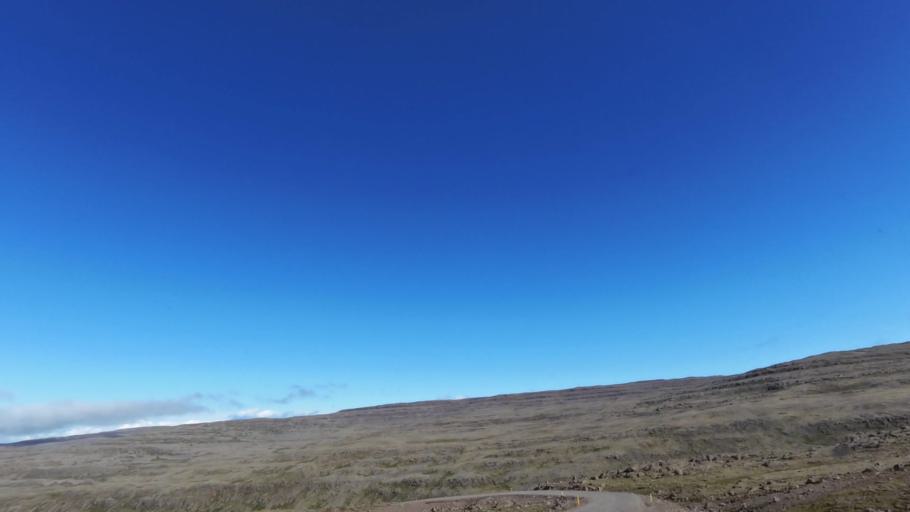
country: IS
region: West
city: Olafsvik
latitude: 65.5509
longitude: -24.2110
